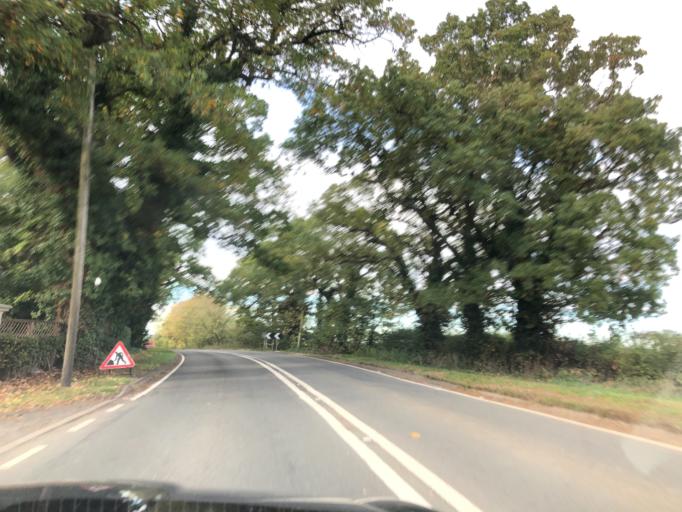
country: GB
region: England
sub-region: Warwickshire
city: Warwick
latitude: 52.2517
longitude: -1.5592
